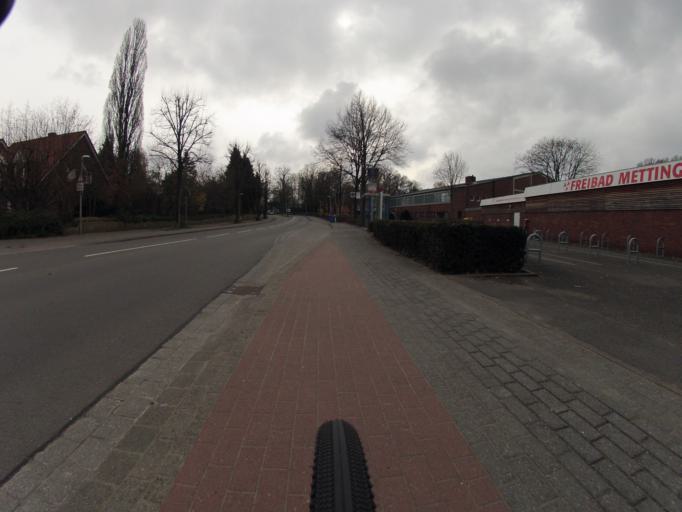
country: DE
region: North Rhine-Westphalia
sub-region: Regierungsbezirk Munster
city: Mettingen
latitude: 52.3254
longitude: 7.7756
